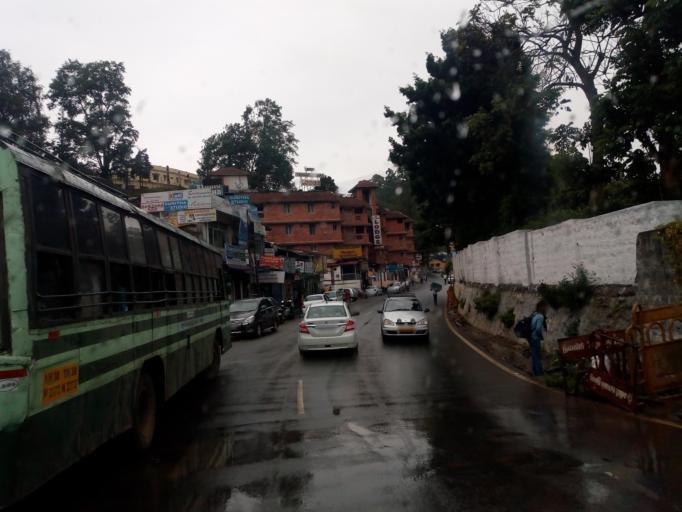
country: IN
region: Tamil Nadu
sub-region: Nilgiri
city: Wellington
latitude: 11.3435
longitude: 76.7931
